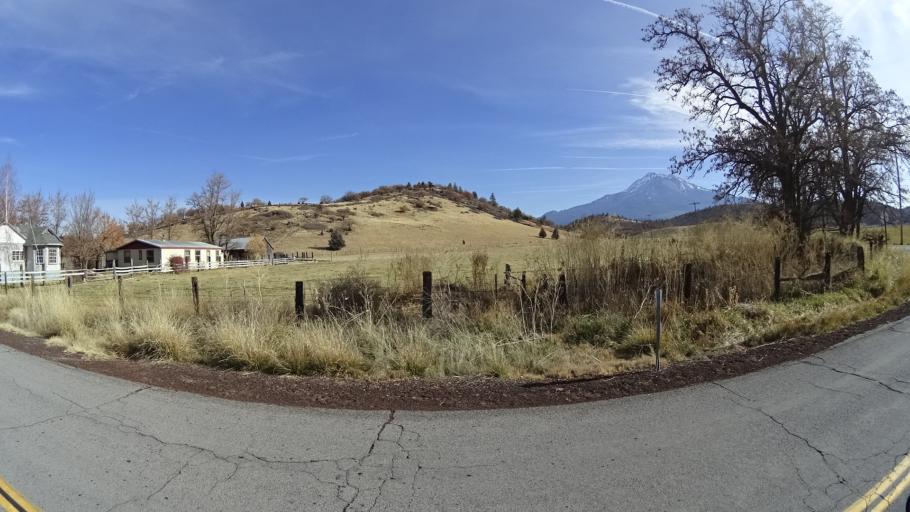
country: US
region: California
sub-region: Siskiyou County
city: Weed
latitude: 41.4685
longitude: -122.4338
